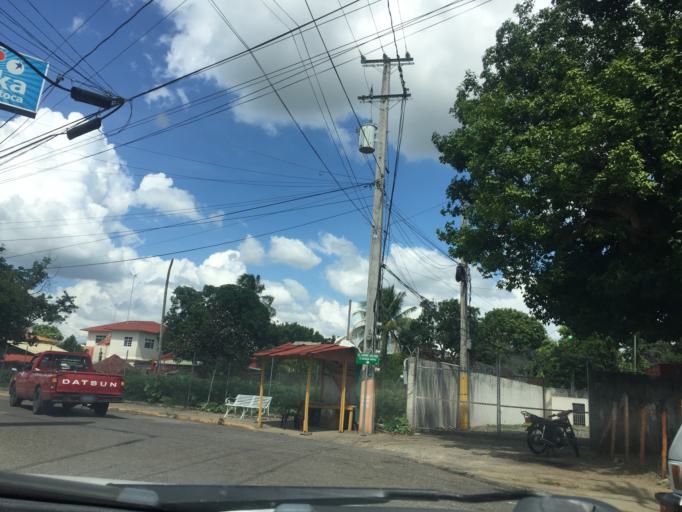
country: DO
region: Santiago
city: Licey al Medio
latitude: 19.3823
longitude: -70.6054
